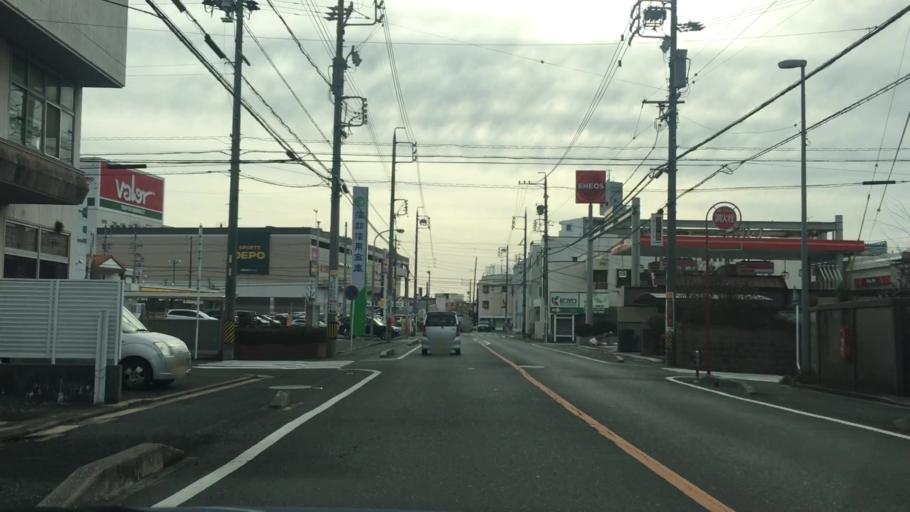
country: JP
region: Aichi
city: Toyohashi
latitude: 34.7558
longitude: 137.3937
